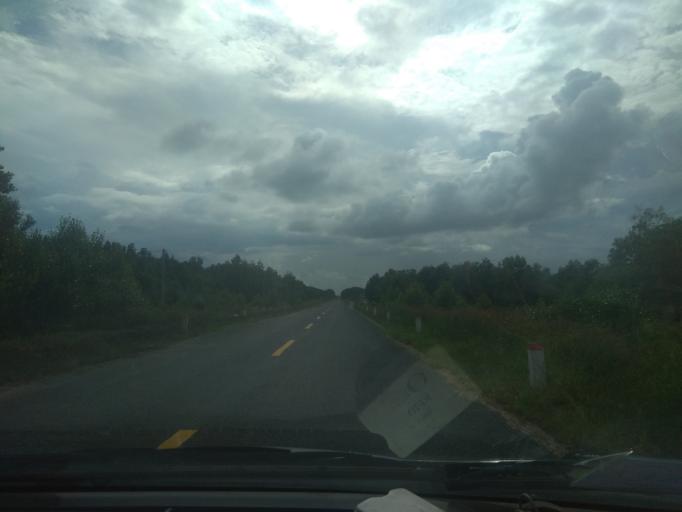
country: VN
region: Ca Mau
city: Ngoc Hien
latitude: 8.5933
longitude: 104.9377
